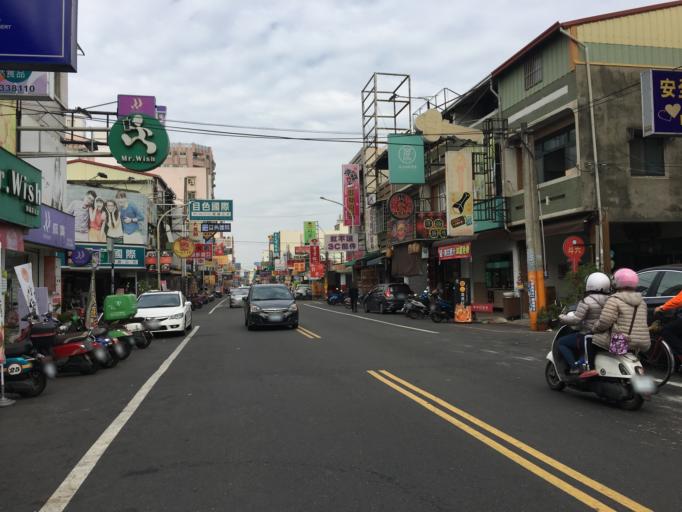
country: TW
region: Taiwan
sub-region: Yunlin
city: Douliu
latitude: 23.7016
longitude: 120.5384
